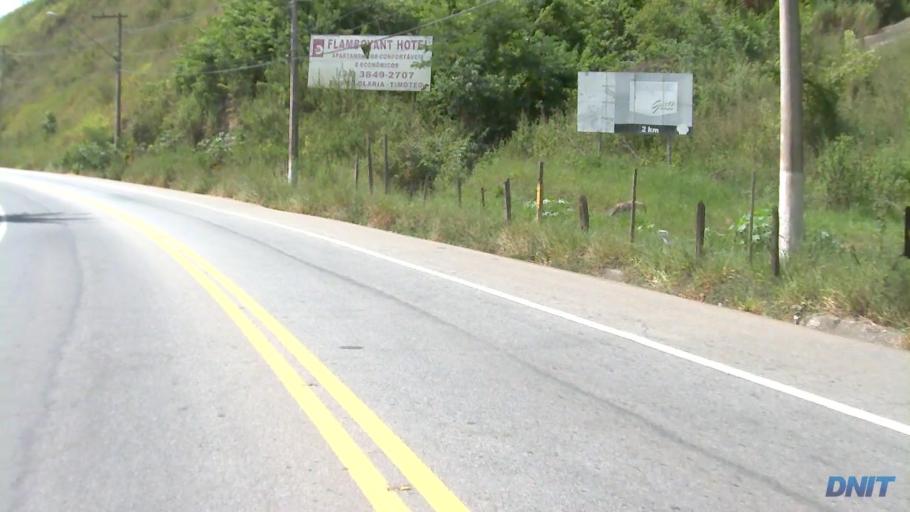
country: BR
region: Minas Gerais
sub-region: Timoteo
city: Timoteo
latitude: -19.5422
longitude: -42.6730
